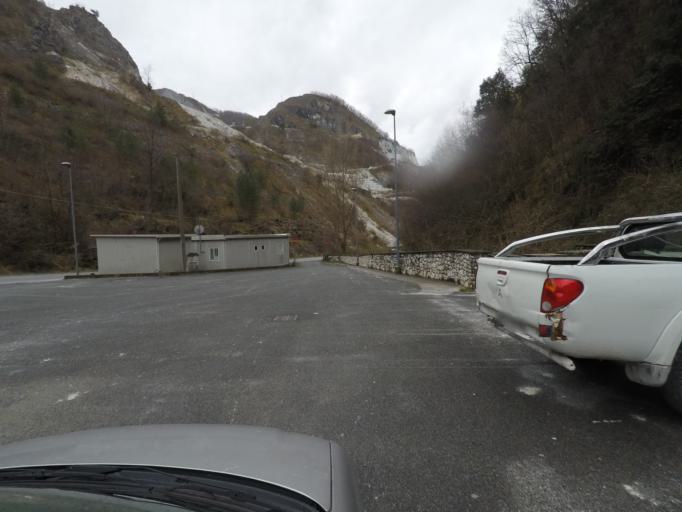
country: IT
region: Tuscany
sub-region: Provincia di Massa-Carrara
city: Montignoso
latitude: 44.0843
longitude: 10.1521
